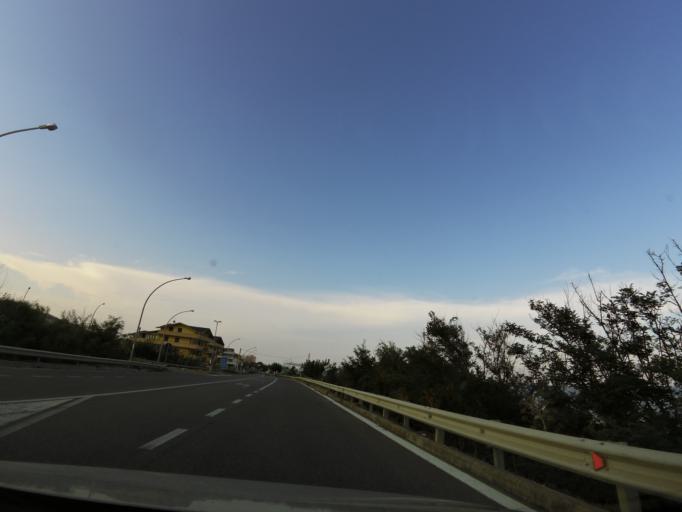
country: IT
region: Calabria
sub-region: Provincia di Reggio Calabria
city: Monasterace Marina
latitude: 38.4277
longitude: 16.5705
